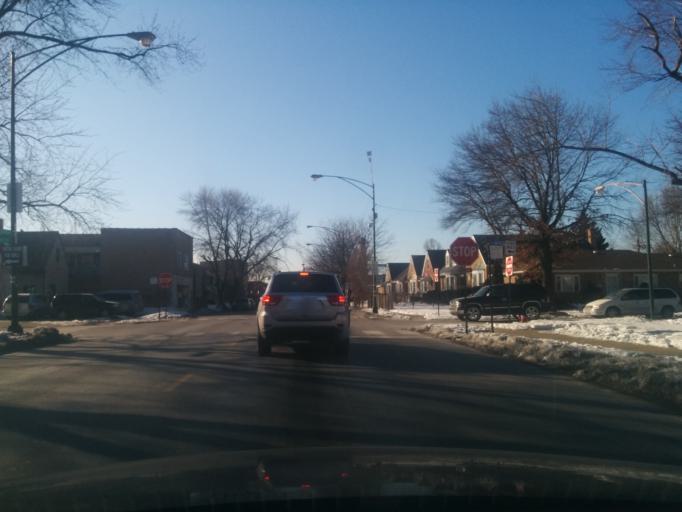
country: US
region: Illinois
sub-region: Cook County
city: Elmwood Park
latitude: 41.9369
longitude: -87.7762
